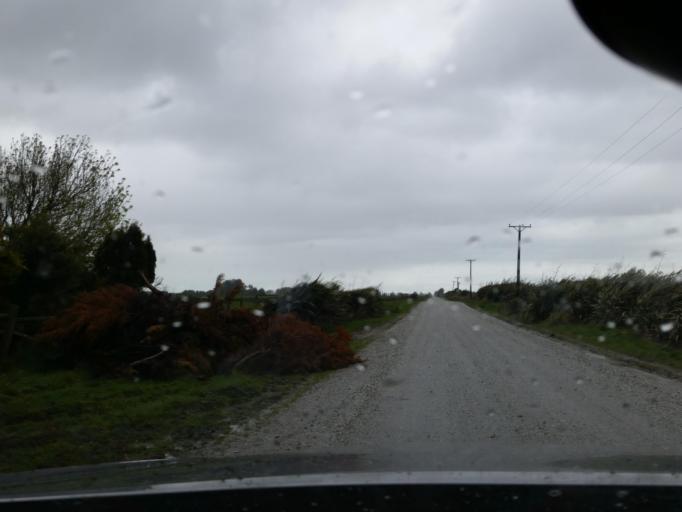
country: NZ
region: Southland
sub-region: Invercargill City
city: Invercargill
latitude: -46.4458
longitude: 168.5062
